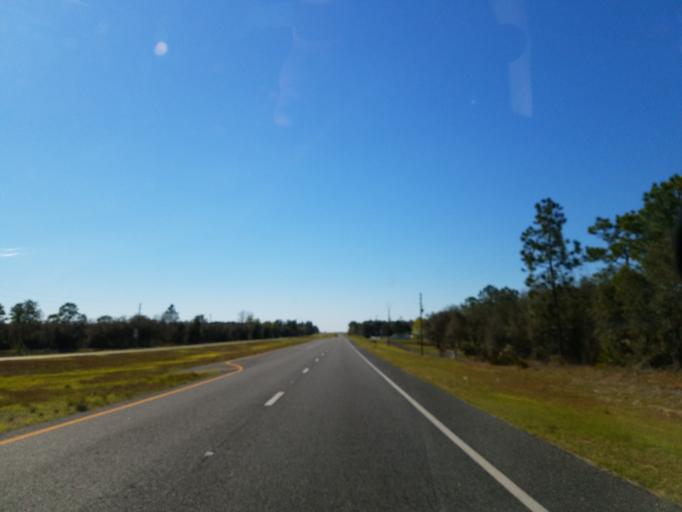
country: US
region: Florida
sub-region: Levy County
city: East Bronson
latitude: 29.4228
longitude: -82.5799
